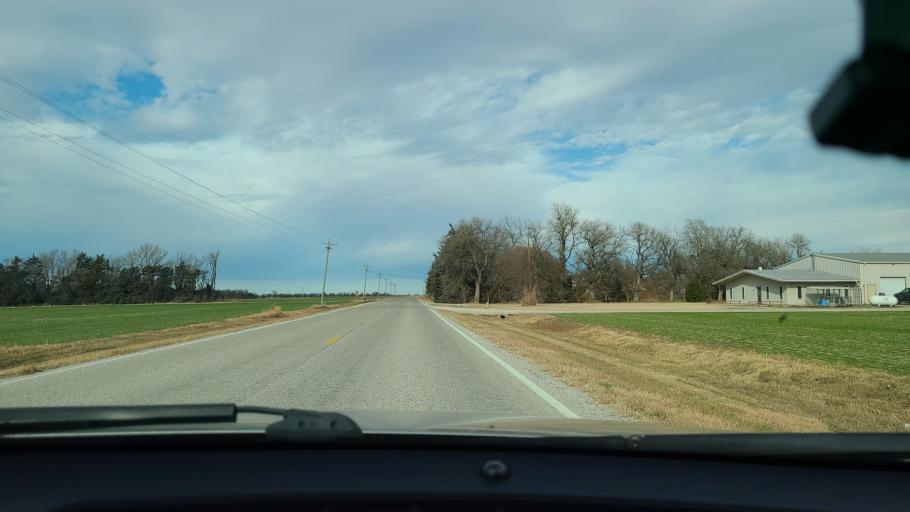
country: US
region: Kansas
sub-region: McPherson County
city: Inman
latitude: 38.3133
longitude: -97.9248
